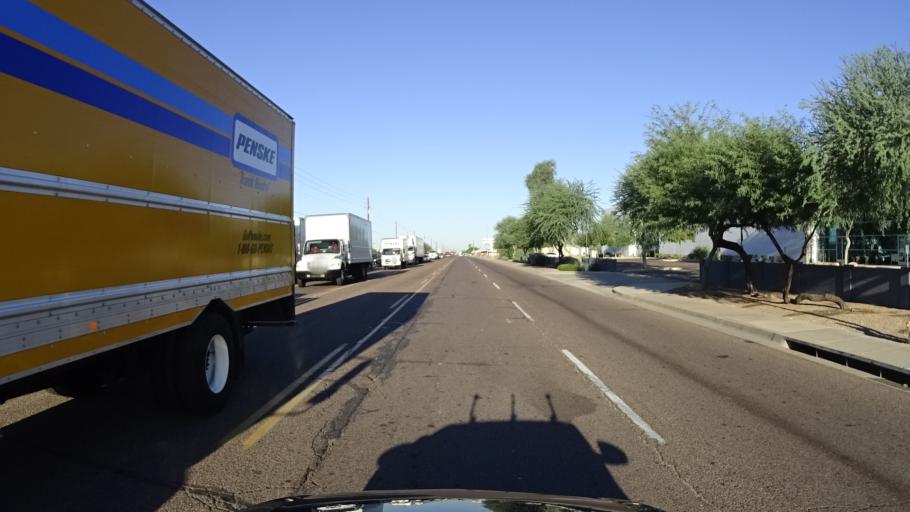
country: US
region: Arizona
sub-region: Maricopa County
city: Laveen
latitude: 33.4369
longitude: -112.1779
